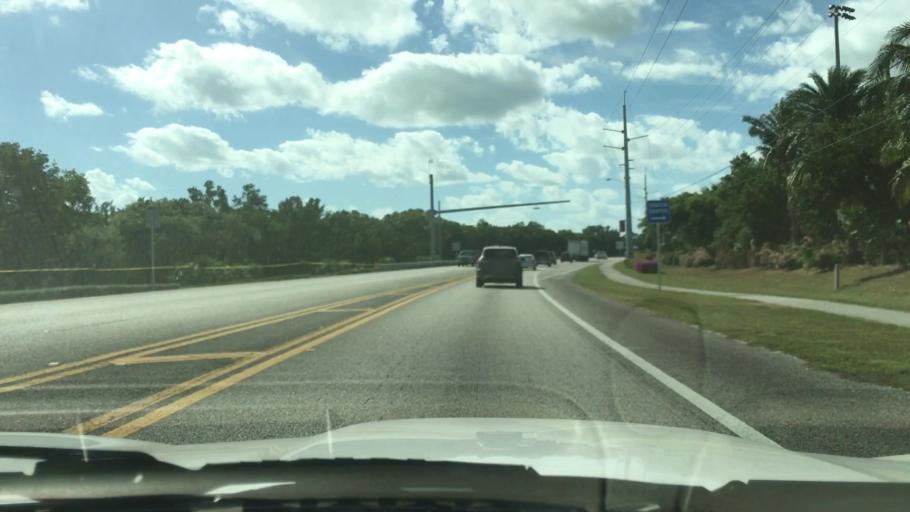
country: US
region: Florida
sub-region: Monroe County
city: Plantation
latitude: 24.9615
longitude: -80.5662
